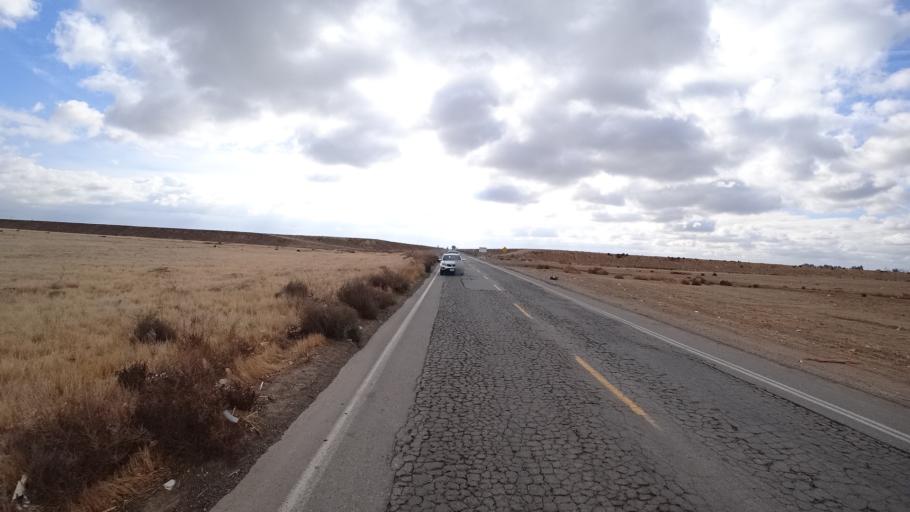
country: US
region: California
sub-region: Kern County
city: Bakersfield
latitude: 35.3404
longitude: -118.9677
